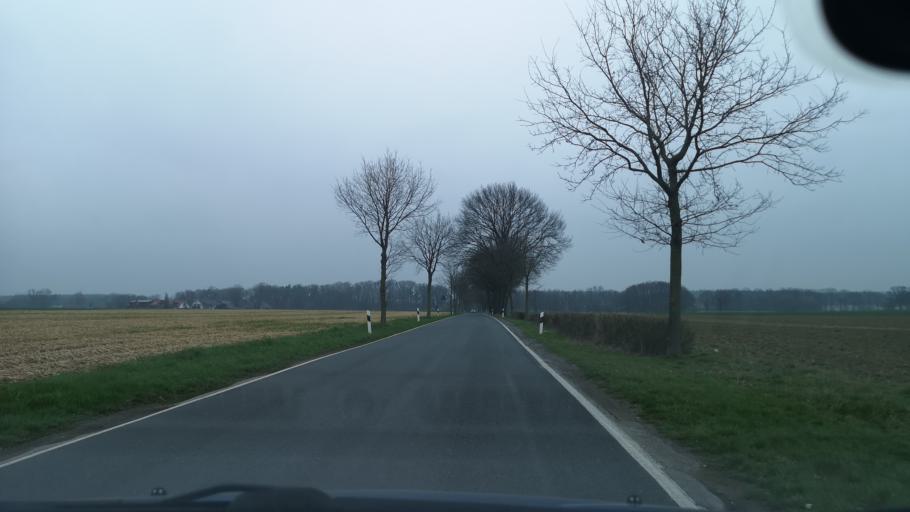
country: DE
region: Lower Saxony
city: Neustadt am Rubenberge
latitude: 52.5686
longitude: 9.4415
